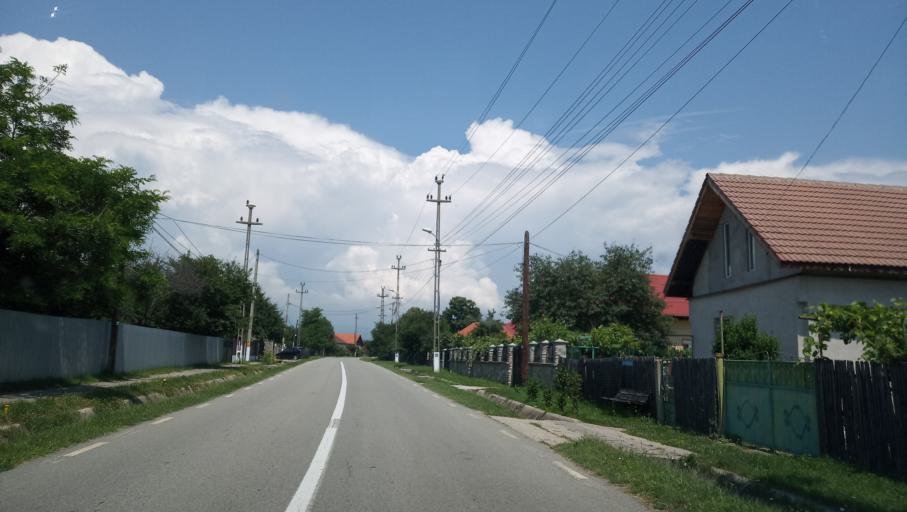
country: RO
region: Gorj
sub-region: Comuna Turcinesti
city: Turcinesti
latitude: 45.0644
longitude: 23.3480
